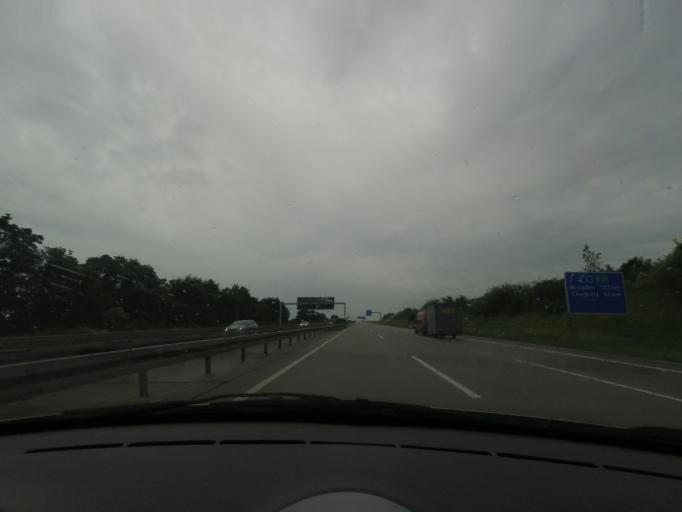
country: DE
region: Thuringia
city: Schwaara
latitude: 50.8954
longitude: 12.1391
